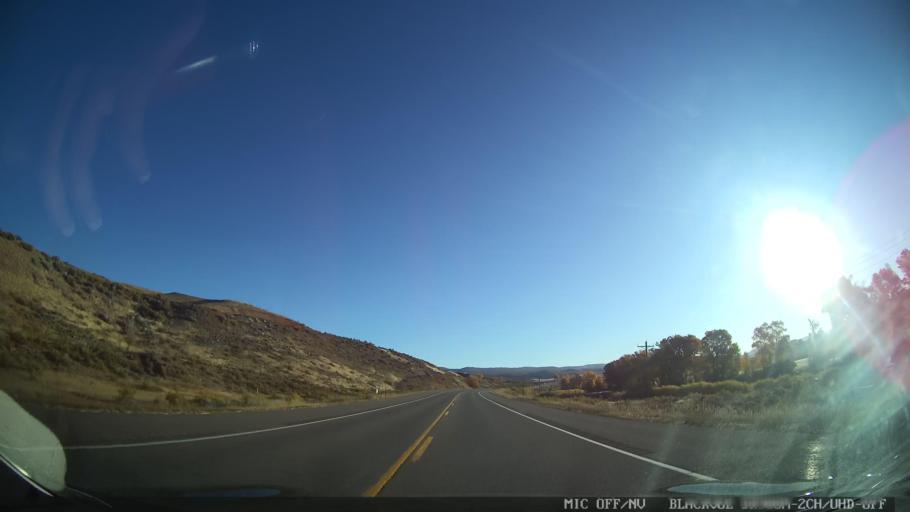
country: US
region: Colorado
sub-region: Grand County
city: Hot Sulphur Springs
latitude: 40.0641
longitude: -106.2374
